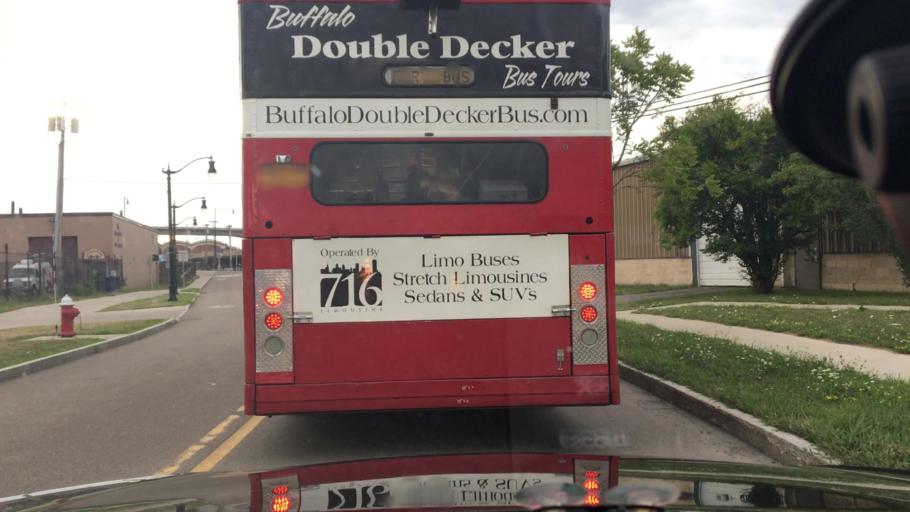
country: US
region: New York
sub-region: Erie County
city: Buffalo
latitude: 42.8715
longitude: -78.8707
